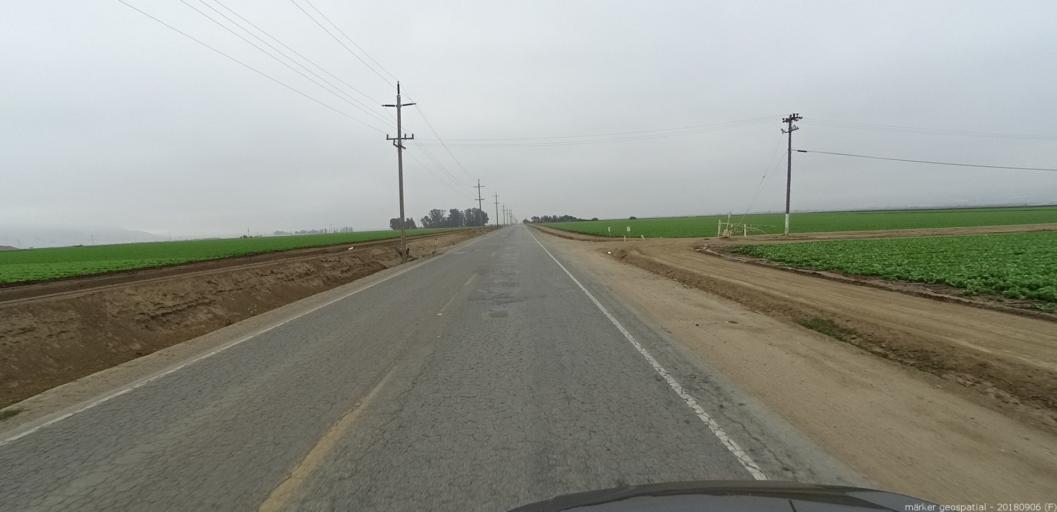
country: US
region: California
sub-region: Monterey County
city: Salinas
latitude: 36.6694
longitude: -121.5982
